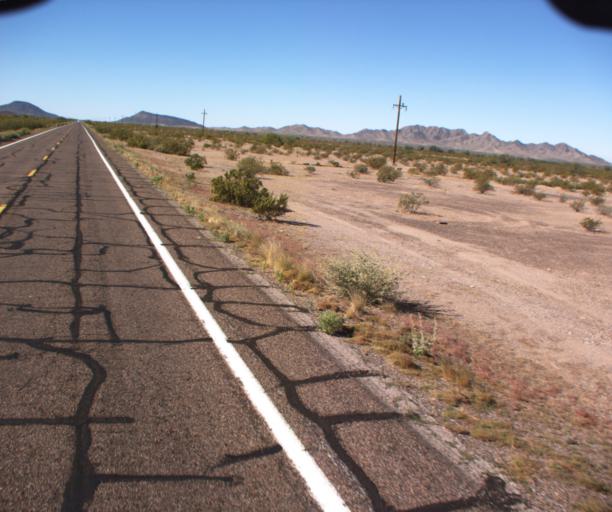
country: US
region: Arizona
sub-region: Maricopa County
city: Gila Bend
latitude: 32.8295
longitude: -112.7832
